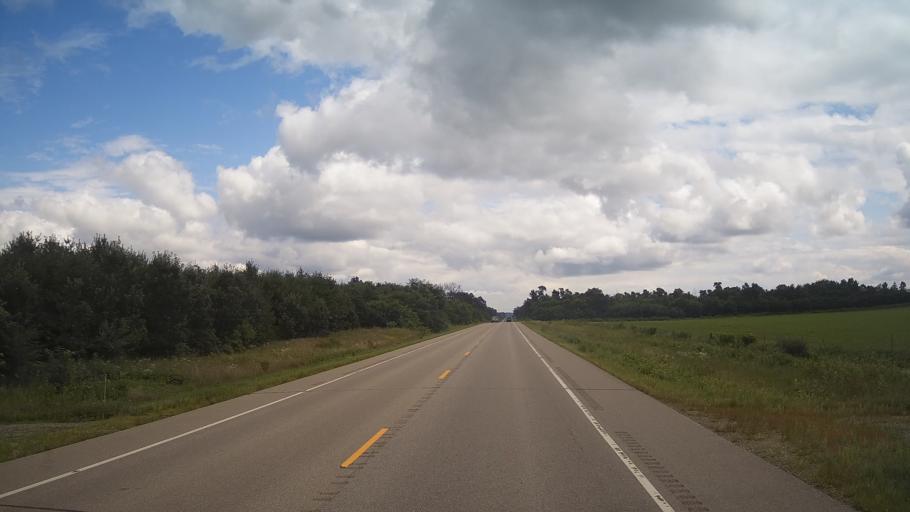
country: US
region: Wisconsin
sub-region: Adams County
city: Friendship
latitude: 44.0219
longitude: -89.6529
